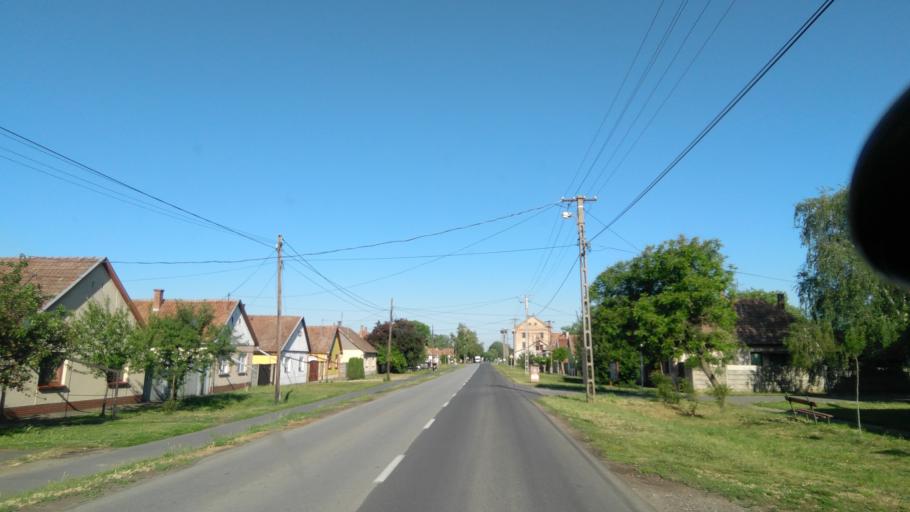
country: HU
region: Bekes
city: Elek
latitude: 46.5319
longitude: 21.2430
